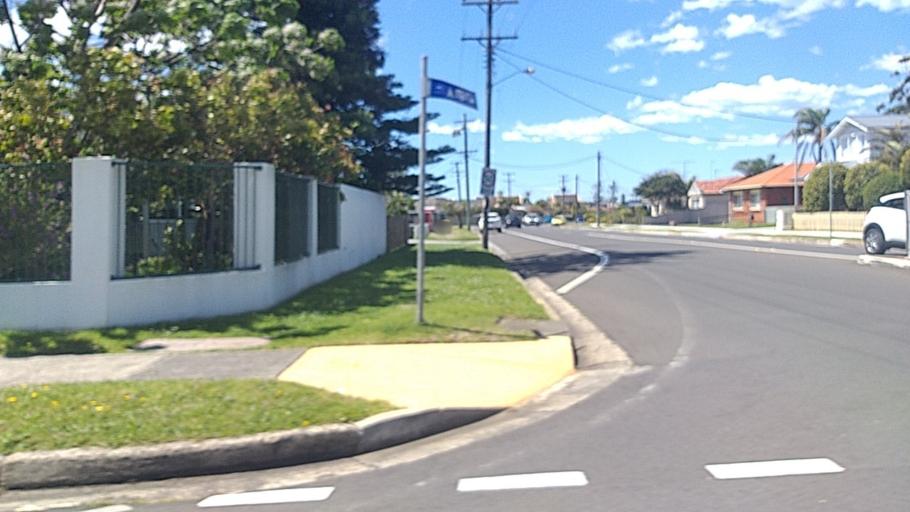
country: AU
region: New South Wales
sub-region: Wollongong
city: East Corrimal
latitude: -34.3791
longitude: 150.9081
